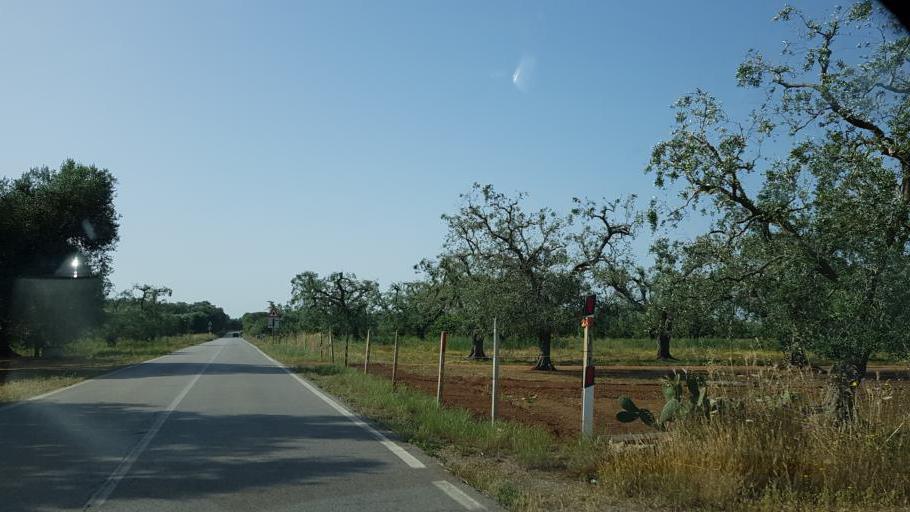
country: IT
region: Apulia
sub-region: Provincia di Brindisi
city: Mesagne
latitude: 40.5203
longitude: 17.8228
